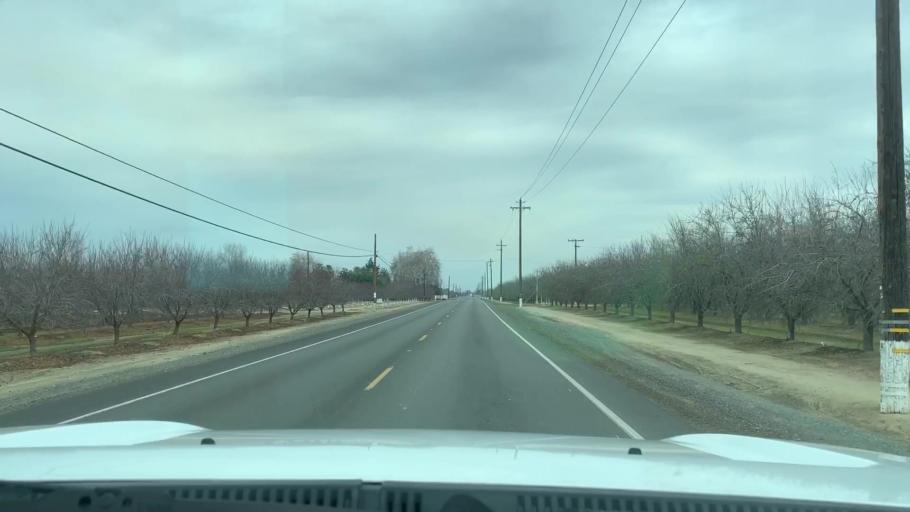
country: US
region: California
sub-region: Kern County
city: Shafter
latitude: 35.4007
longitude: -119.2520
